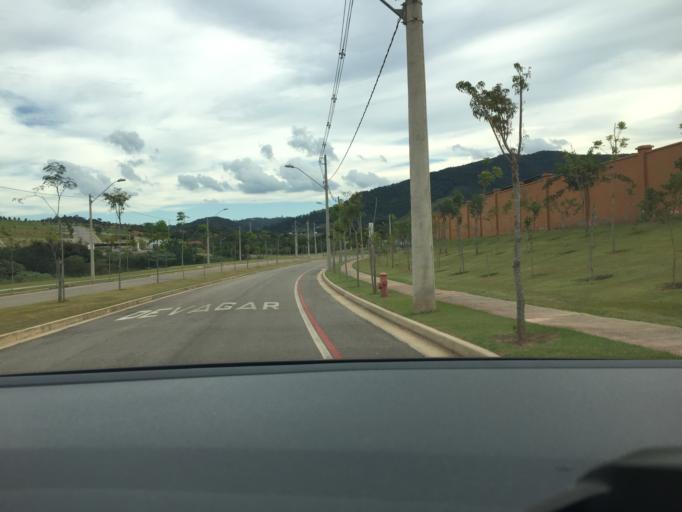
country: BR
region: Sao Paulo
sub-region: Jundiai
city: Jundiai
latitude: -23.2324
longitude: -46.8776
